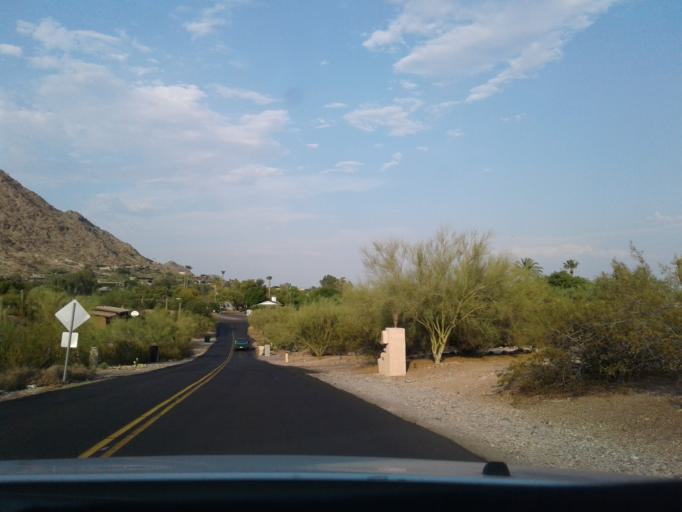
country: US
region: Arizona
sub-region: Maricopa County
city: Paradise Valley
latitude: 33.5383
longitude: -111.9784
